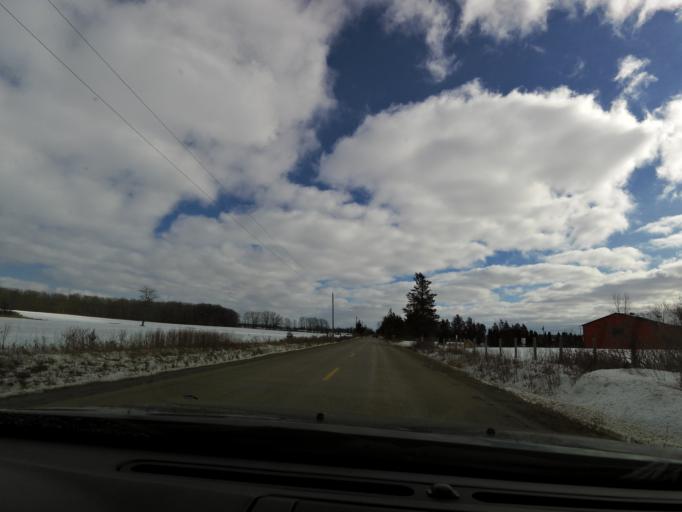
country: CA
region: Ontario
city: Hamilton
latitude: 43.1077
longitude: -79.6316
